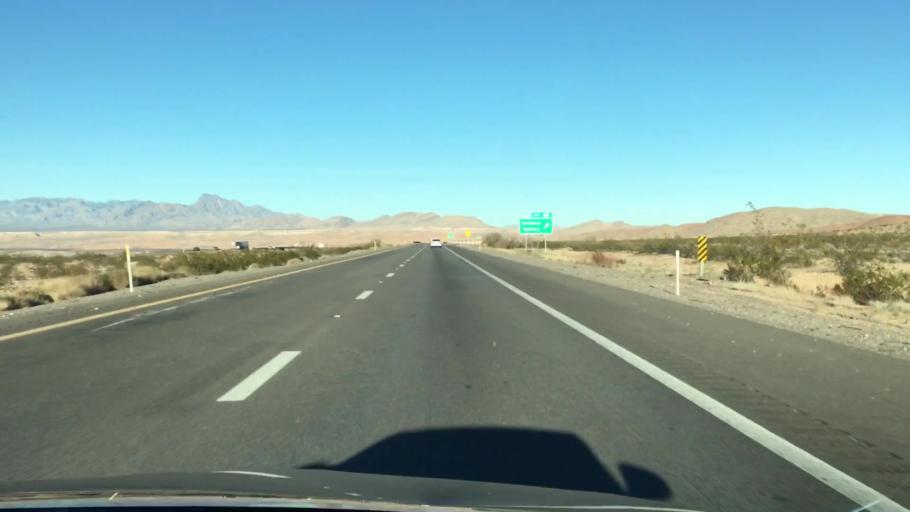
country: US
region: Nevada
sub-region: Clark County
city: Moapa Town
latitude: 36.6332
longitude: -114.6031
